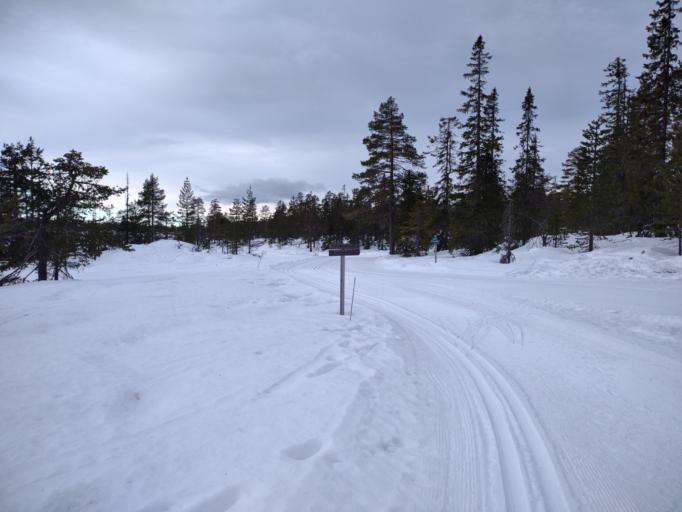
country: NO
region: Buskerud
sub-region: Flesberg
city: Lampeland
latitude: 59.7549
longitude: 9.4723
